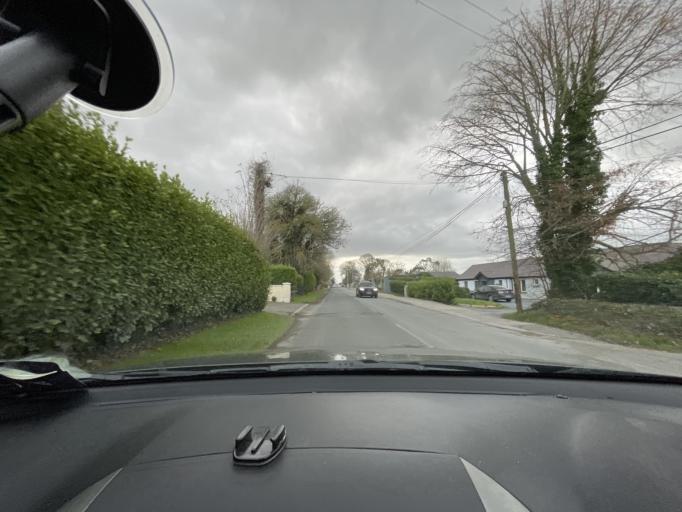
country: IE
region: Leinster
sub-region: Lu
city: Termonfeckin
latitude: 53.7580
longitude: -6.2749
